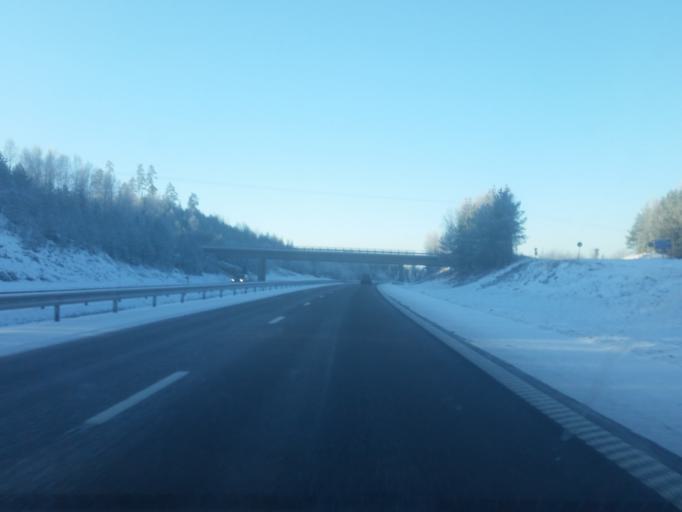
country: SE
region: Vaestra Goetaland
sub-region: Bollebygds Kommun
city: Bollebygd
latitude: 57.6678
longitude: 12.6076
